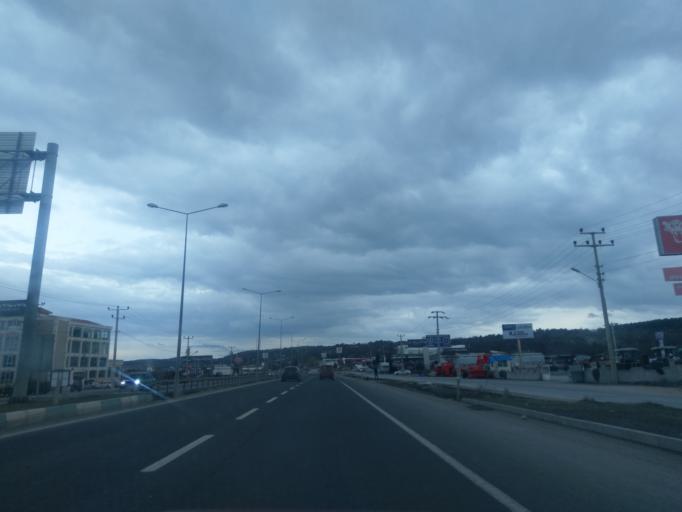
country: TR
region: Kuetahya
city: Kutahya
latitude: 39.3823
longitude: 30.0453
